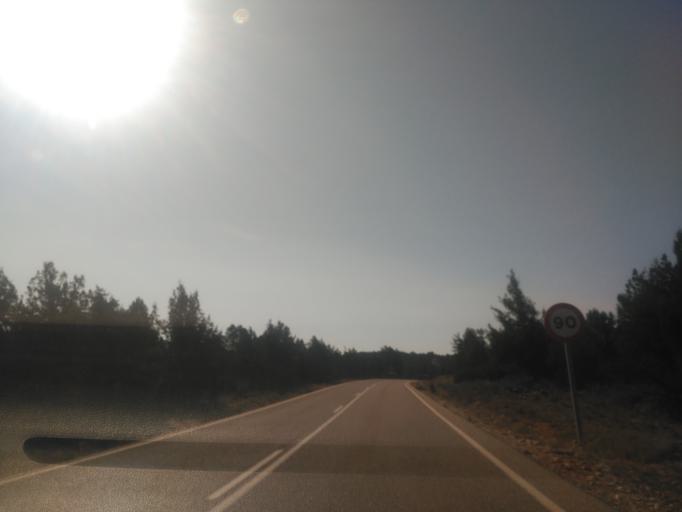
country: ES
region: Castille and Leon
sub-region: Provincia de Soria
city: Ucero
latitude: 41.7339
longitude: -3.0425
